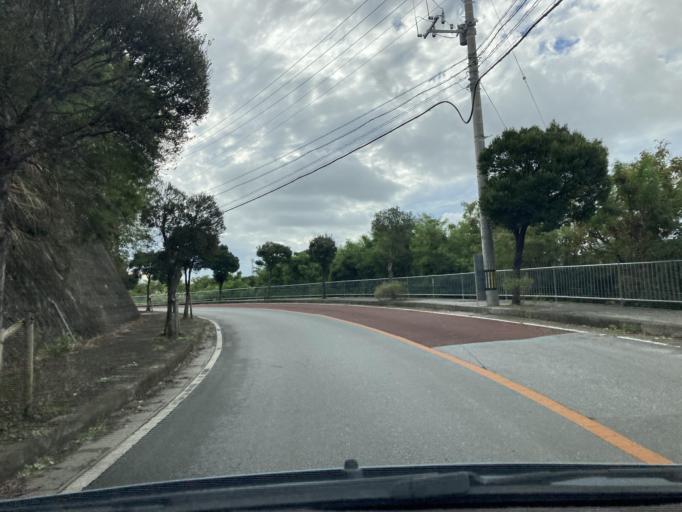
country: JP
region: Okinawa
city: Tomigusuku
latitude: 26.1830
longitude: 127.7468
